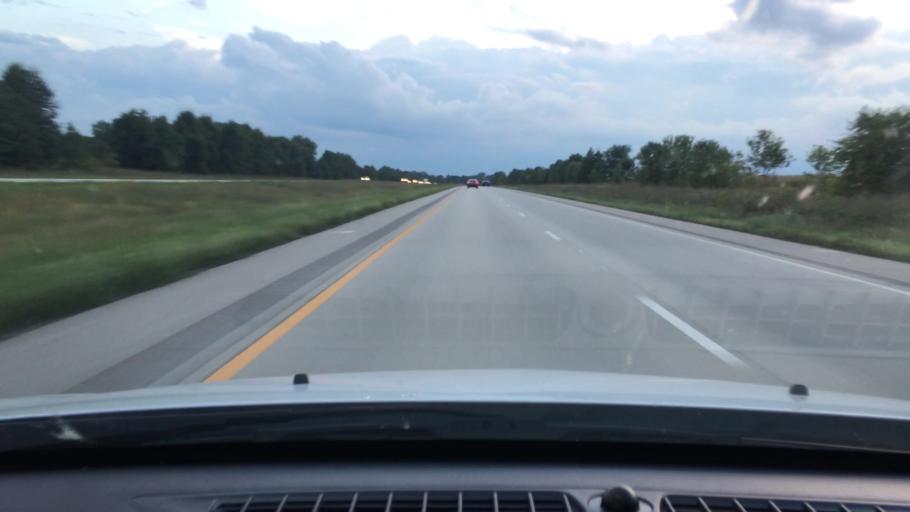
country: US
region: Illinois
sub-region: Sangamon County
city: New Berlin
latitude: 39.7476
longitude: -89.8103
